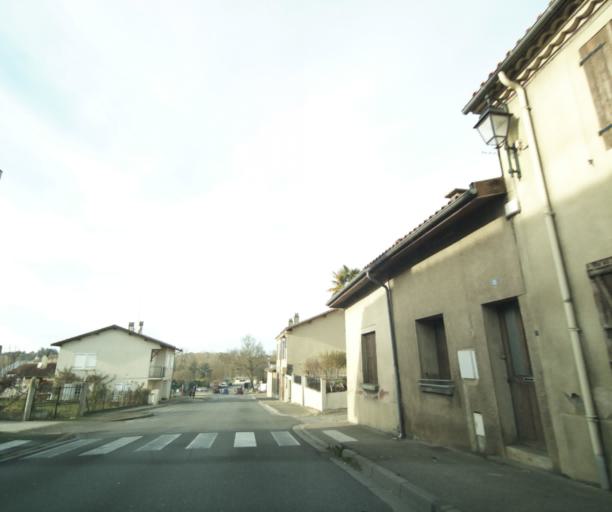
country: FR
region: Midi-Pyrenees
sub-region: Departement du Gers
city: Gimont
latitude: 43.6291
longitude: 0.8746
